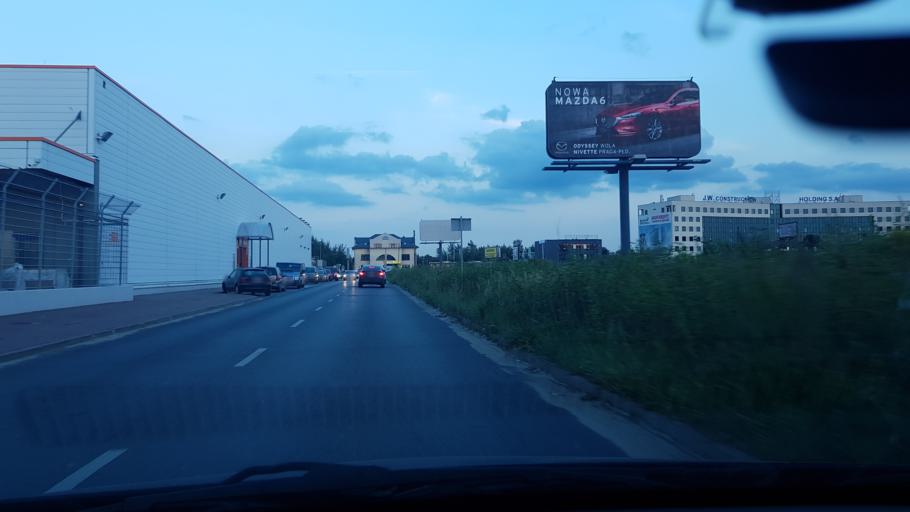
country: PL
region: Masovian Voivodeship
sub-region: Powiat wolominski
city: Zabki
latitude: 52.3024
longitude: 21.0851
